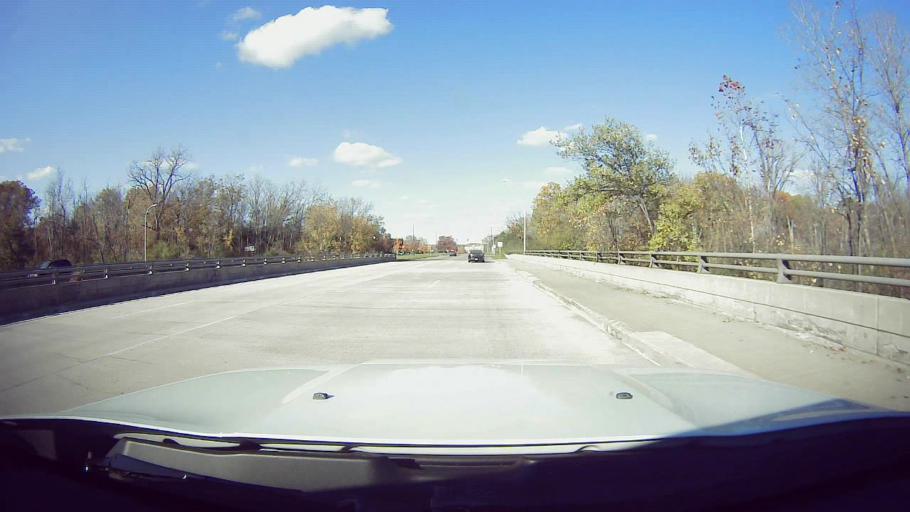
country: US
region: Michigan
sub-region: Wayne County
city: Dearborn
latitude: 42.3105
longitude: -83.2262
